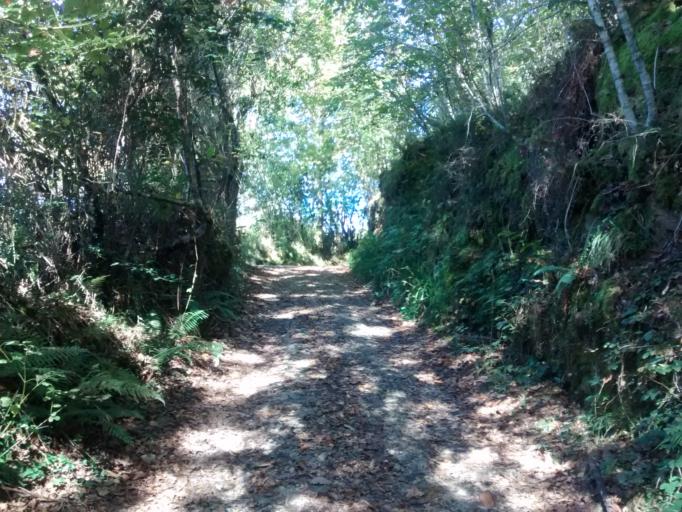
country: ES
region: Asturias
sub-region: Province of Asturias
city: Colunga
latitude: 43.4636
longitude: -5.2374
